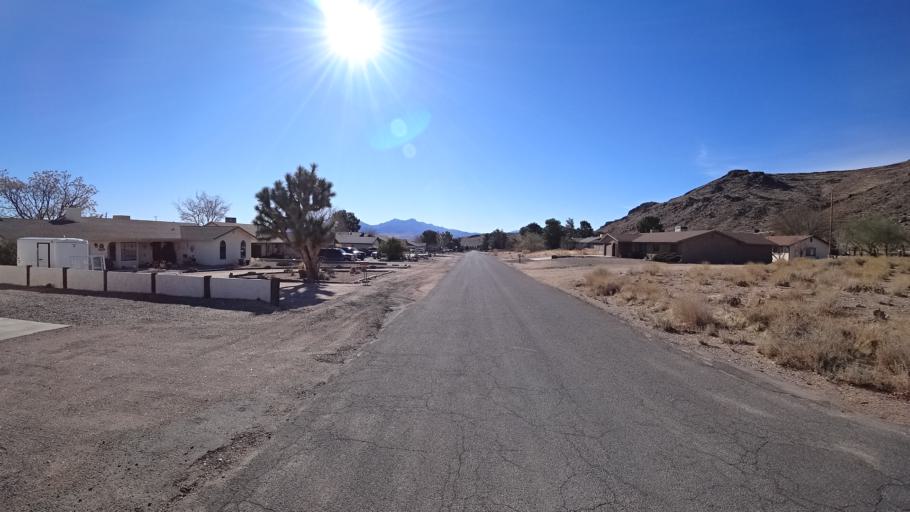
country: US
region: Arizona
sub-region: Mohave County
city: New Kingman-Butler
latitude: 35.2674
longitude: -114.0486
